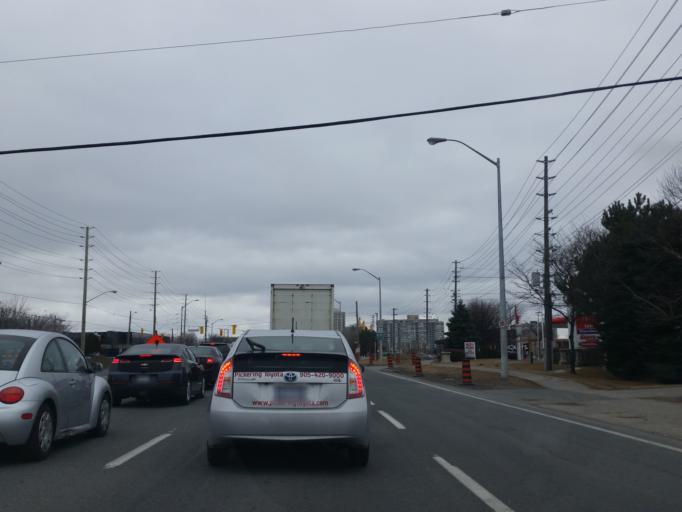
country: CA
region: Ontario
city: Ajax
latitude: 43.8346
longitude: -79.0918
